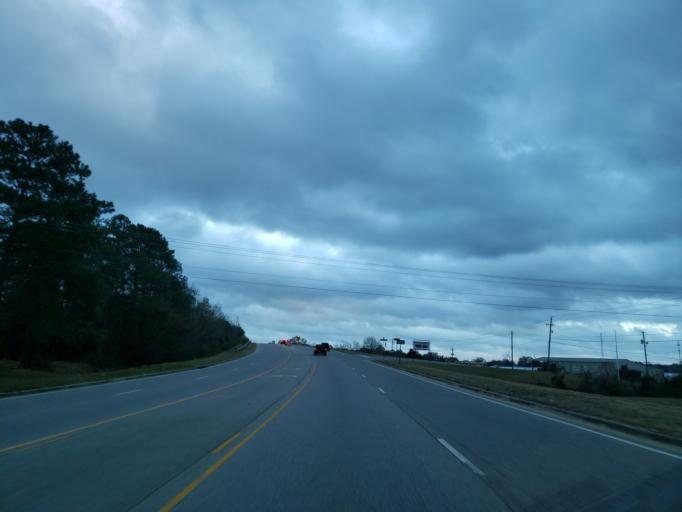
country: US
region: Alabama
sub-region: Mobile County
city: Prichard
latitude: 30.7791
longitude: -88.2660
